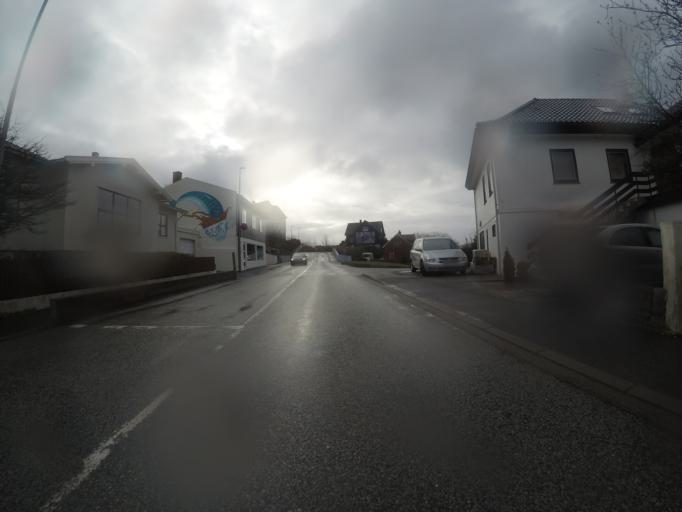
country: FO
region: Streymoy
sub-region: Torshavn
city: Torshavn
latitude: 62.0118
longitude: -6.7706
